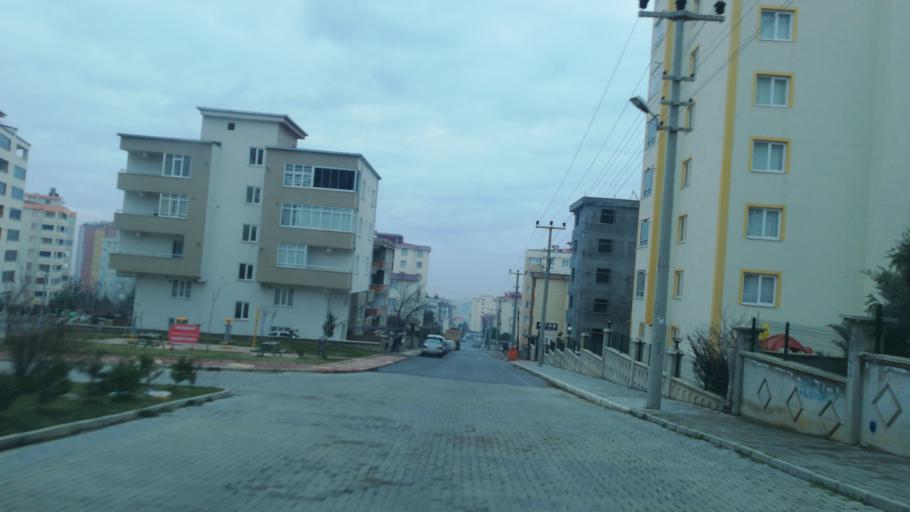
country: TR
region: Kahramanmaras
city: Kahramanmaras
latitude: 37.5976
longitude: 36.8983
